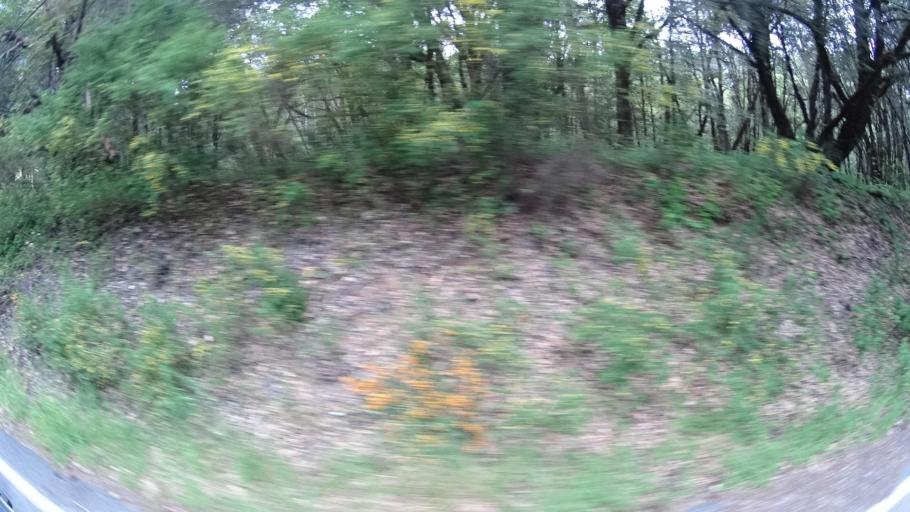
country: US
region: California
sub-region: Humboldt County
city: Redway
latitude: 40.1111
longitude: -123.8956
